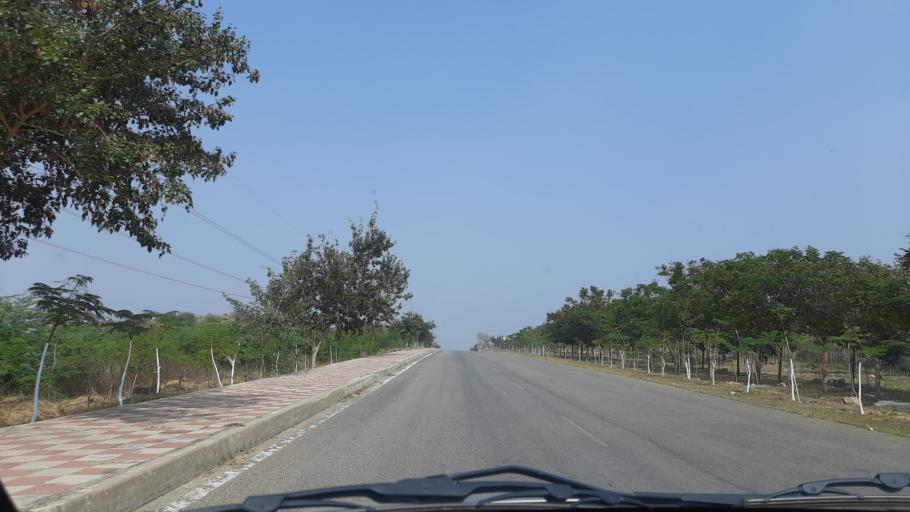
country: IN
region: Telangana
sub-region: Rangareddi
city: Lal Bahadur Nagar
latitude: 17.2934
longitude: 78.6519
